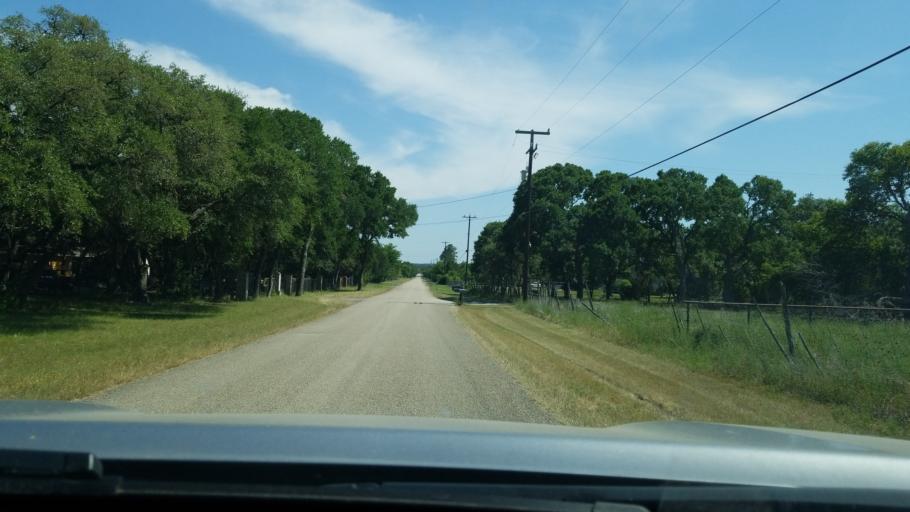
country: US
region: Texas
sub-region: Bexar County
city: Timberwood Park
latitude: 29.7572
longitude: -98.5179
